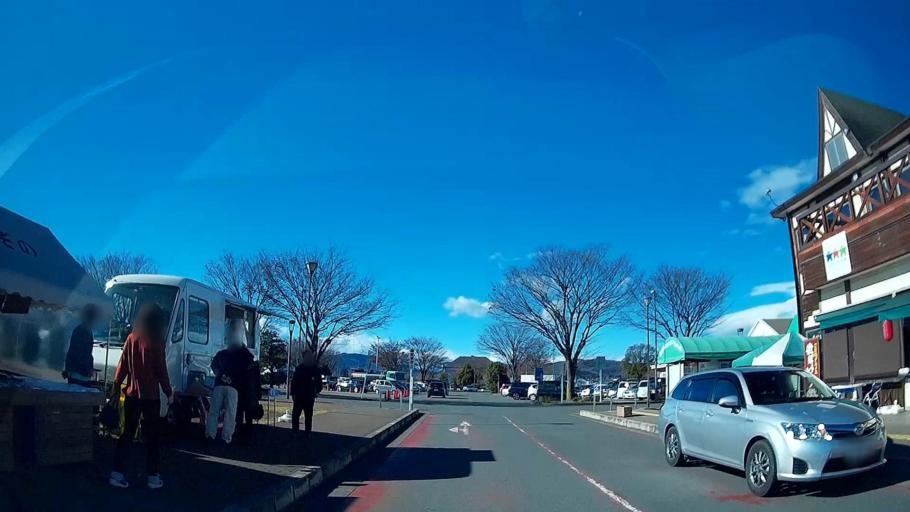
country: JP
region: Saitama
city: Yorii
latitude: 36.1214
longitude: 139.2269
